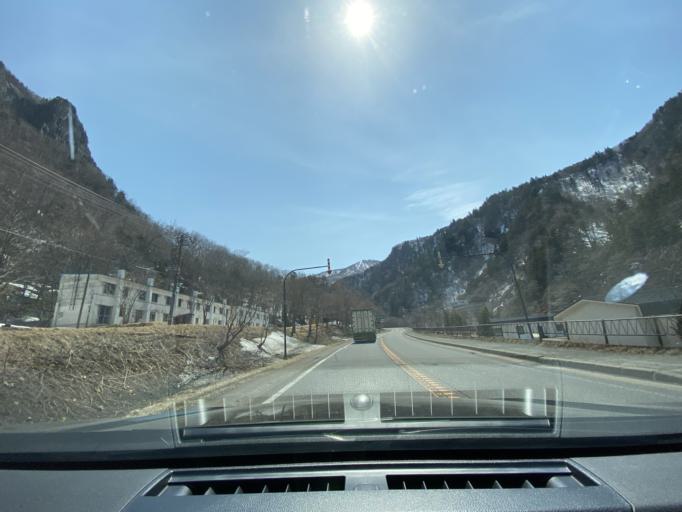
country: JP
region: Hokkaido
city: Kamikawa
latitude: 43.7337
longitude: 142.9423
